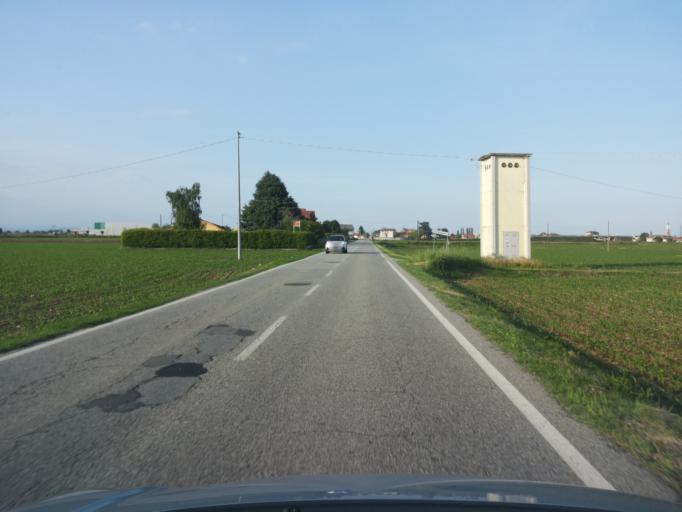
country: IT
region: Piedmont
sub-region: Provincia di Vercelli
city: Tronzano Vercellese
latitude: 45.3372
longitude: 8.1574
